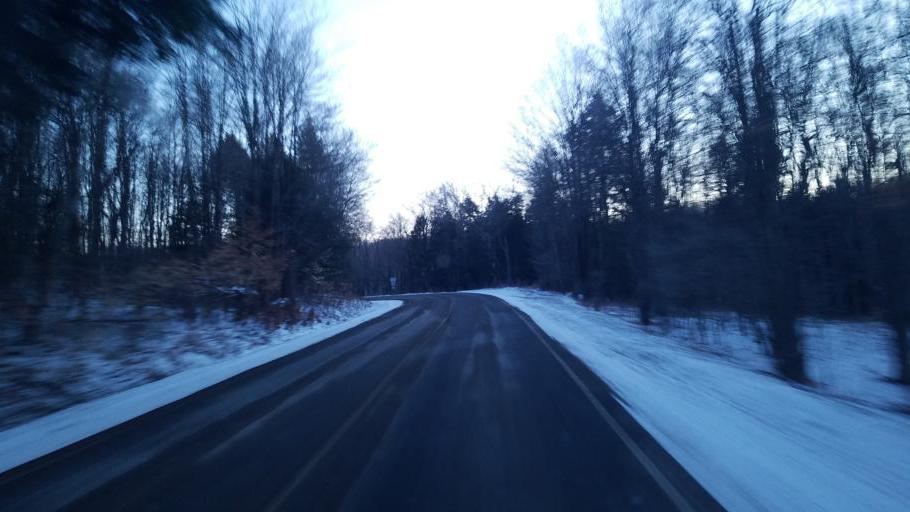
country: US
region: New York
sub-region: Allegany County
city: Andover
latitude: 41.9996
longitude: -77.7694
